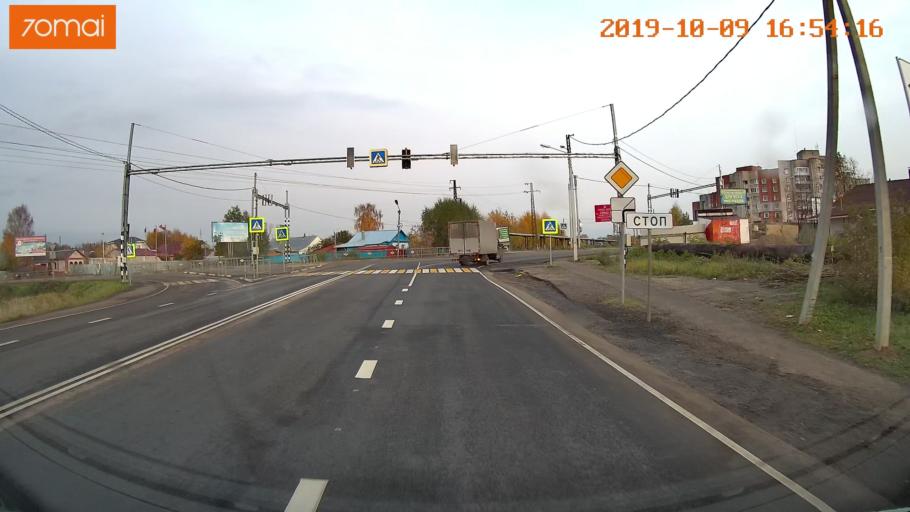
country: RU
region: Ivanovo
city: Privolzhsk
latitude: 57.3746
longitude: 41.2788
